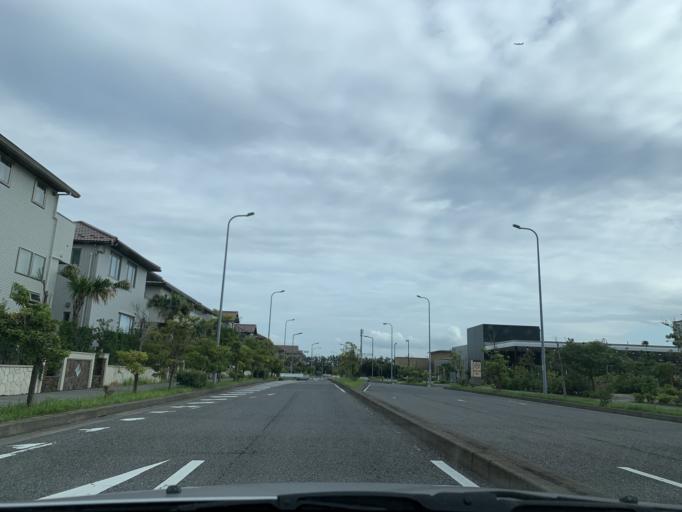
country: JP
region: Tokyo
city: Urayasu
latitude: 35.6424
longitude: 139.9310
